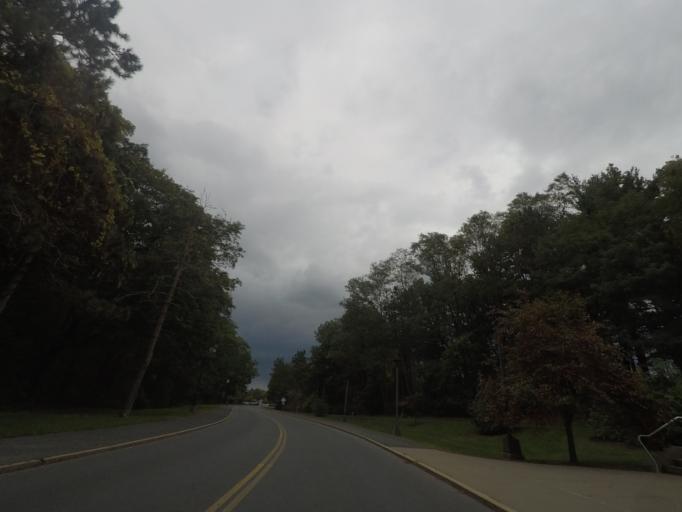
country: US
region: New York
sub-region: Albany County
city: Roessleville
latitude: 42.6814
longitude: -73.8192
